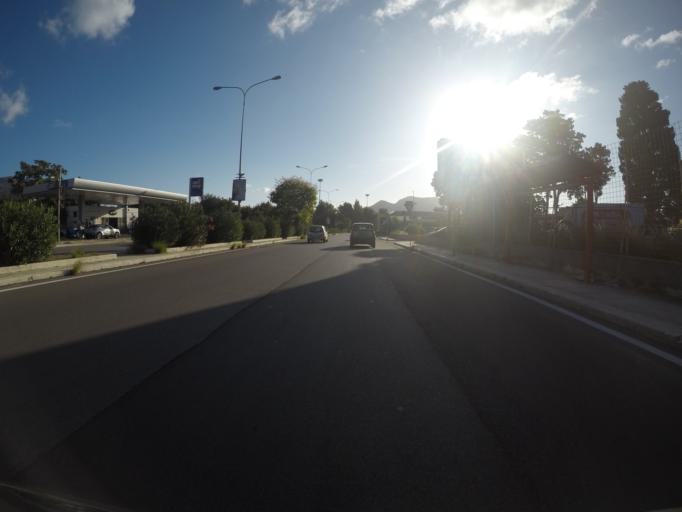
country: IT
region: Sicily
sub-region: Palermo
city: Isola delle Femmine
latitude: 38.1886
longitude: 13.2970
